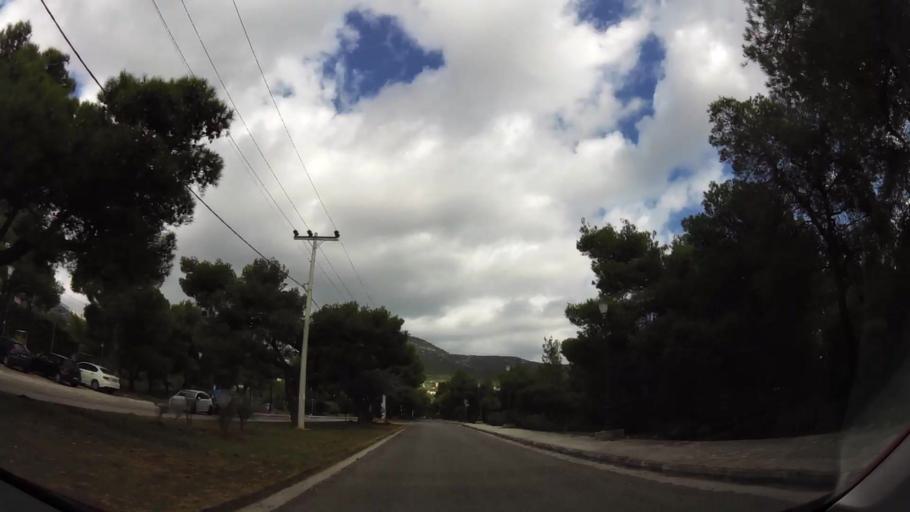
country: GR
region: Attica
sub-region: Nomarchia Anatolikis Attikis
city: Thrakomakedones
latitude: 38.1321
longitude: 23.7571
